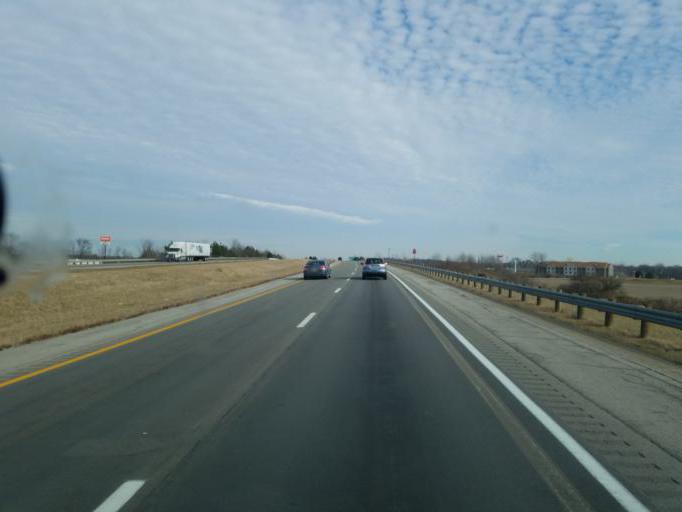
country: US
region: Ohio
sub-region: Montgomery County
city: Brookville
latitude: 39.8422
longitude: -84.4331
